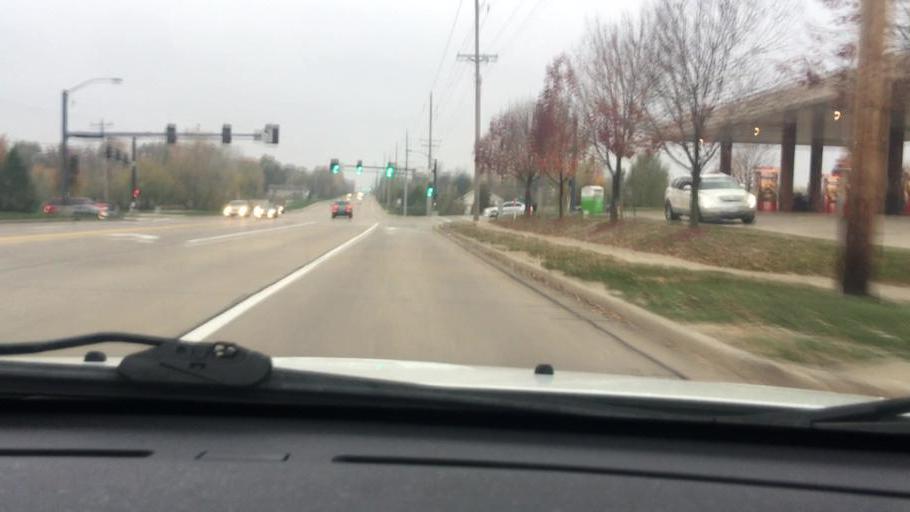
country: US
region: Missouri
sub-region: Saint Charles County
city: O'Fallon
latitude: 38.8218
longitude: -90.6811
